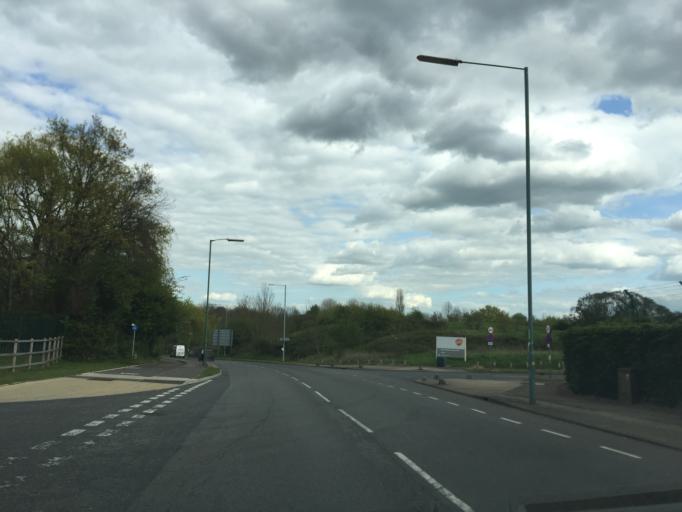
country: GB
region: England
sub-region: Essex
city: Roydon
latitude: 51.7675
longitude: 0.0713
